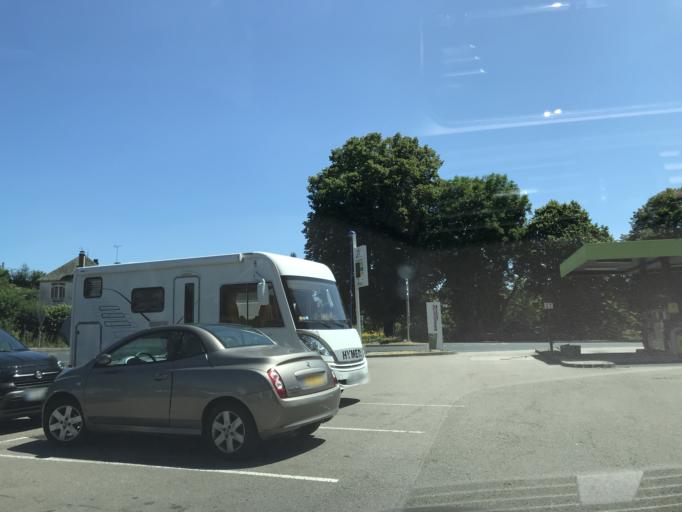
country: FR
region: Limousin
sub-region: Departement de la Correze
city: Neuvic
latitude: 45.3796
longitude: 2.2677
